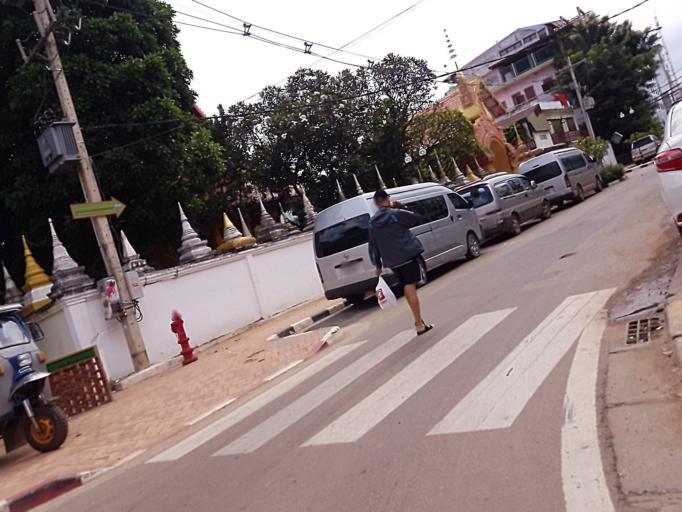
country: LA
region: Vientiane
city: Vientiane
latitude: 17.9657
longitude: 102.6048
